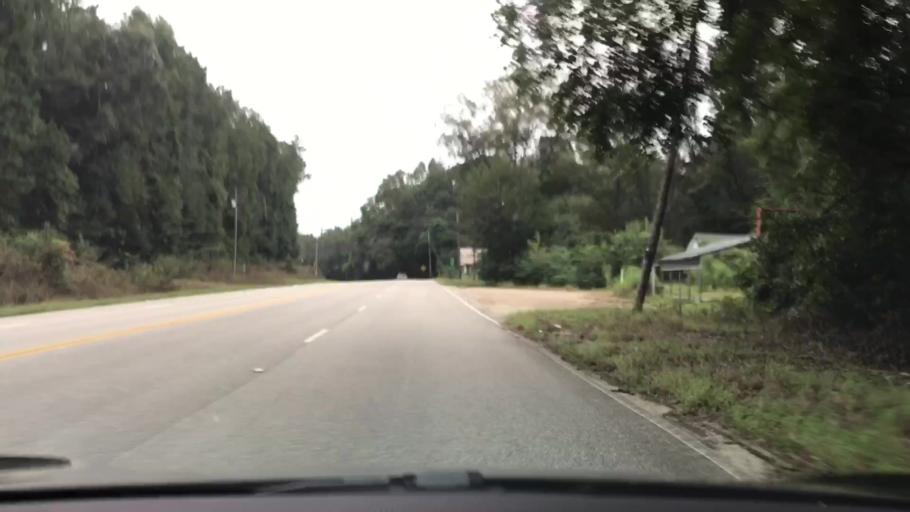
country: US
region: Alabama
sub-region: Coffee County
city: Elba
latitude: 31.4520
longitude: -86.0698
